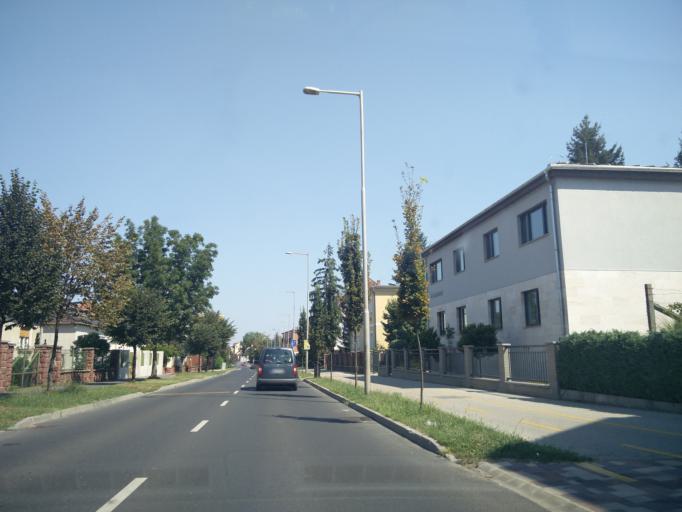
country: HU
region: Zala
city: Zalaegerszeg
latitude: 46.8352
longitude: 16.8402
